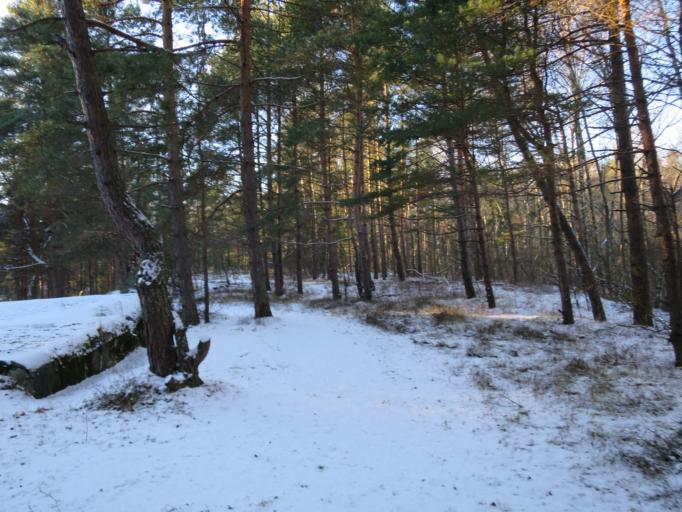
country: LV
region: Riga
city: Daugavgriva
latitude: 57.0671
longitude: 24.0636
